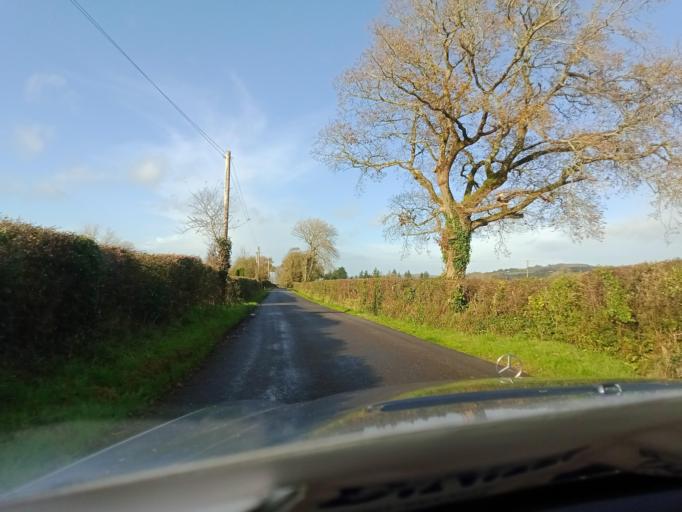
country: IE
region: Leinster
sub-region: Kilkenny
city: Mooncoin
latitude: 52.3304
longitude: -7.2549
